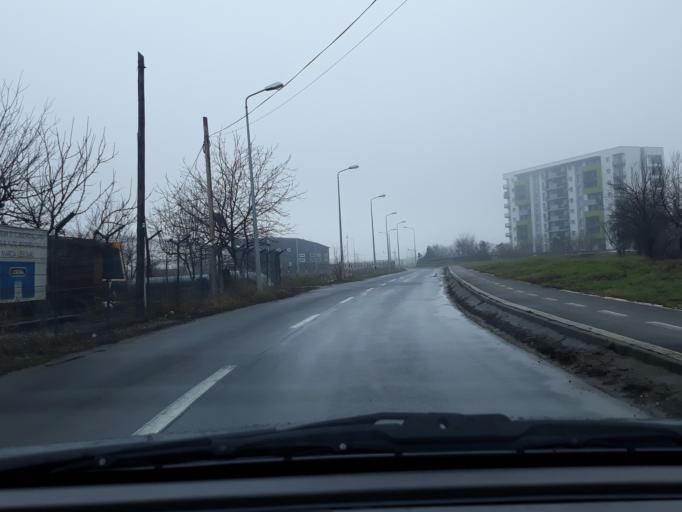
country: RO
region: Bihor
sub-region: Comuna Sanmartin
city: Sanmartin
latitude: 47.0364
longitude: 21.9603
